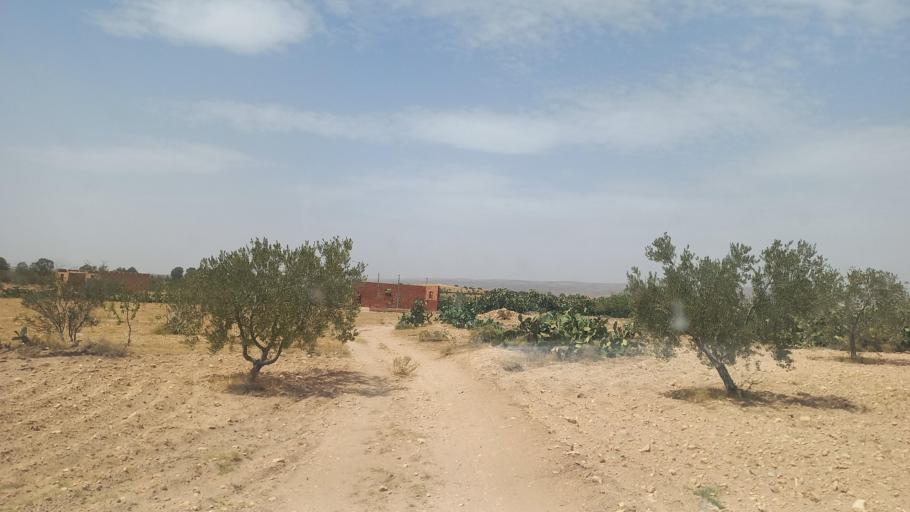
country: TN
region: Al Qasrayn
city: Kasserine
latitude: 35.2644
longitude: 8.9852
